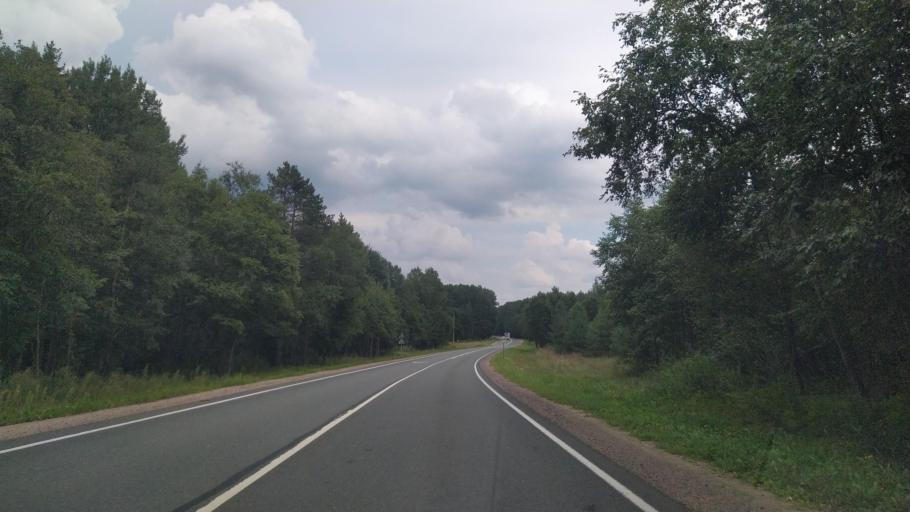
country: RU
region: Pskov
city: Pskov
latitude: 57.8325
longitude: 28.5311
